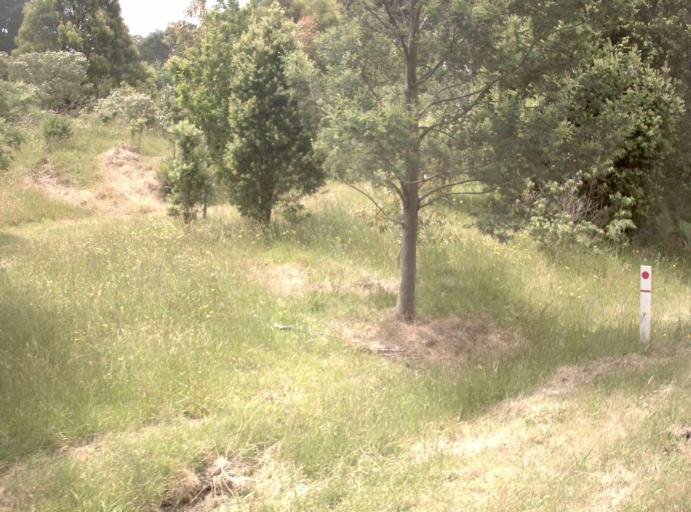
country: AU
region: Victoria
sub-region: Latrobe
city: Traralgon
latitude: -38.4224
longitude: 146.6064
